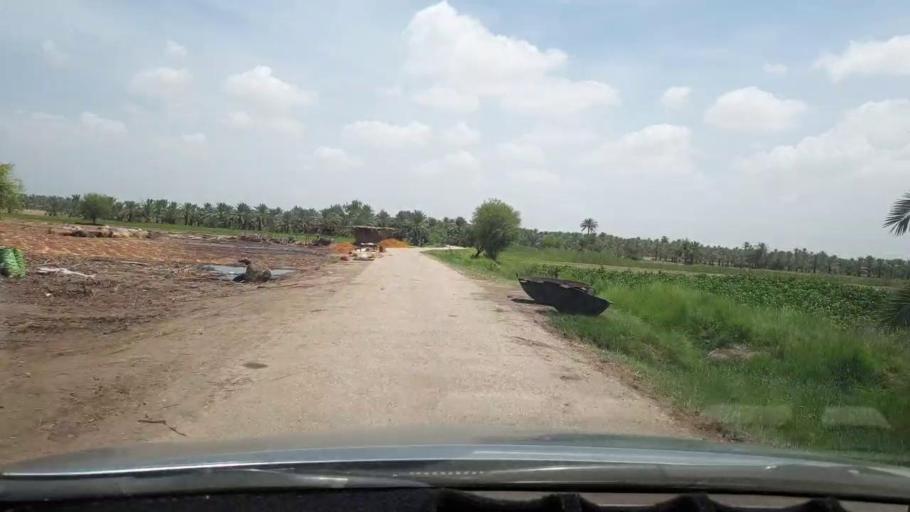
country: PK
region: Sindh
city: Khairpur
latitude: 27.4507
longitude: 68.7831
